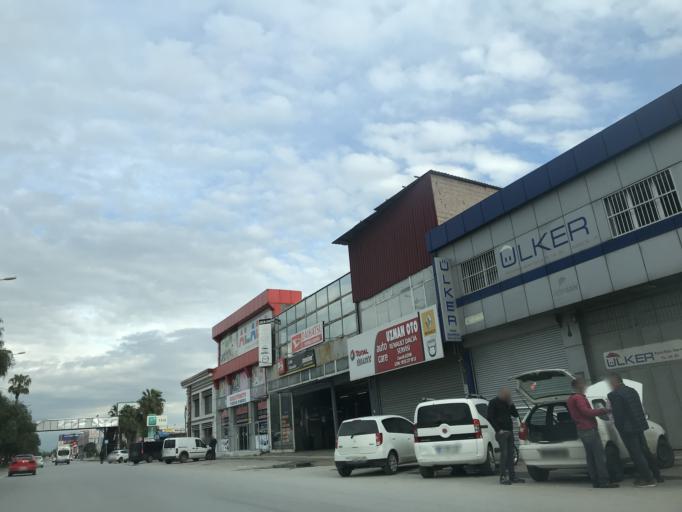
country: TR
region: Adana
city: Seyhan
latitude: 36.9948
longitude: 35.2786
